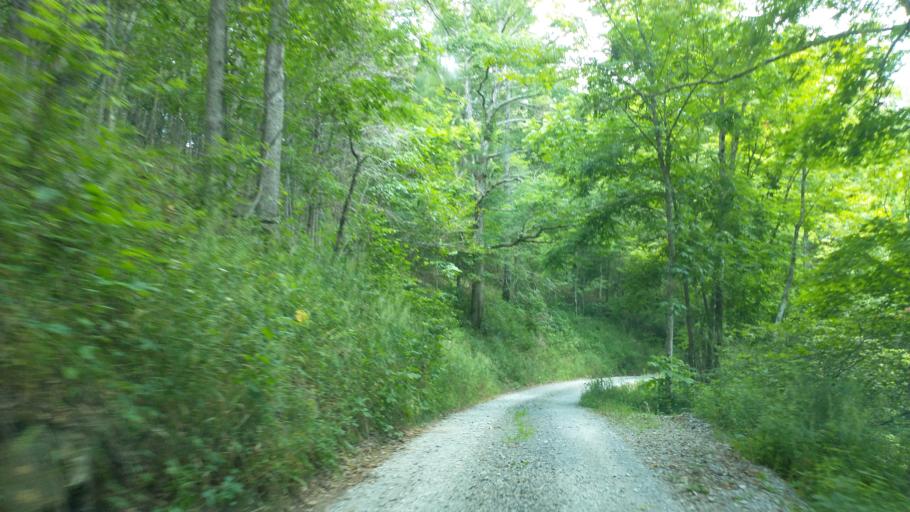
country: US
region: West Virginia
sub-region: Mercer County
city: Athens
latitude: 37.4362
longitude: -81.0015
